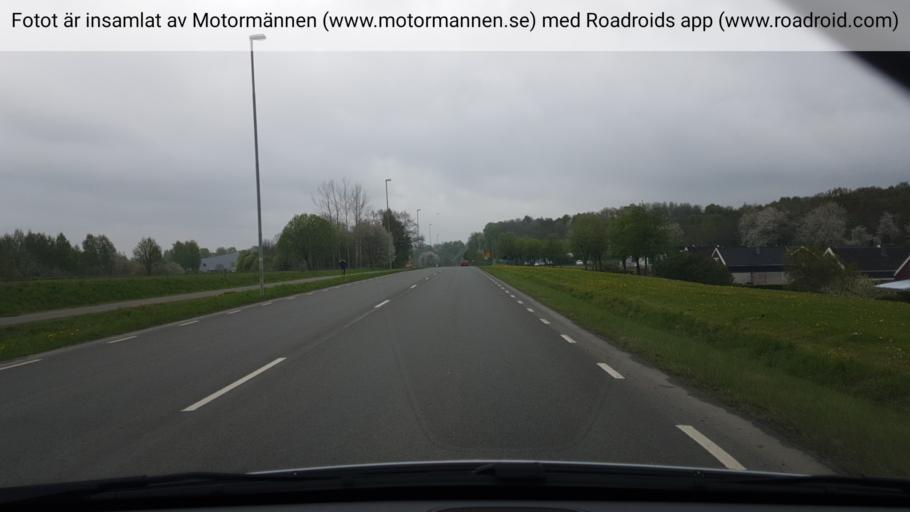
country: SE
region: Vaestra Goetaland
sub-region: Skovde Kommun
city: Skoevde
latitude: 58.4181
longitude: 13.8455
